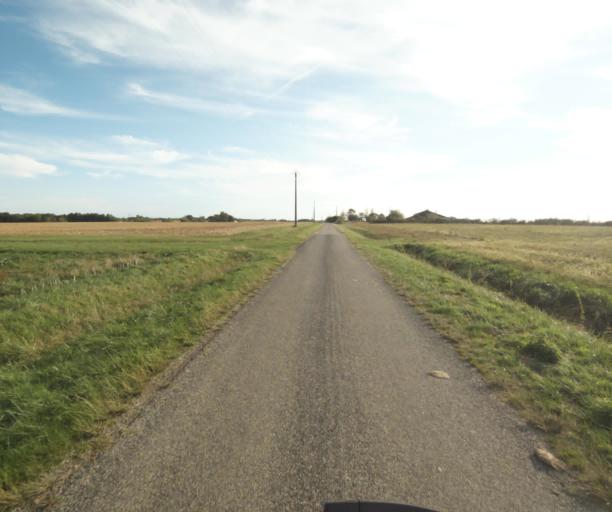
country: FR
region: Midi-Pyrenees
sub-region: Departement du Tarn-et-Garonne
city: Finhan
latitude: 43.9151
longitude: 1.1315
